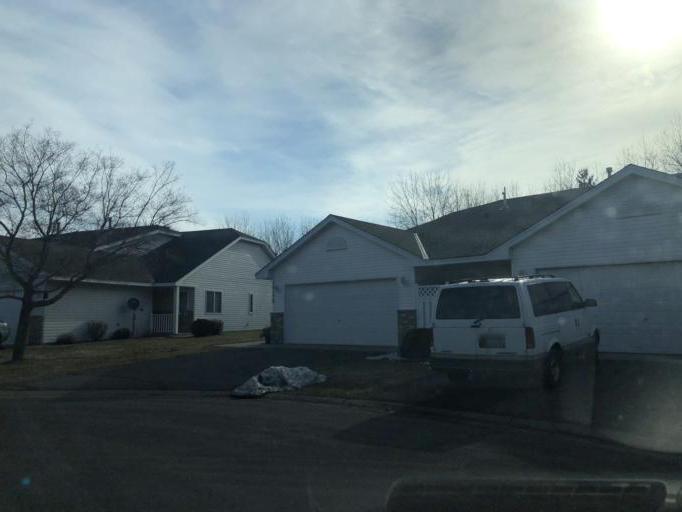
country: US
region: Minnesota
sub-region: Sherburne County
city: Becker
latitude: 45.3930
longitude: -93.8589
